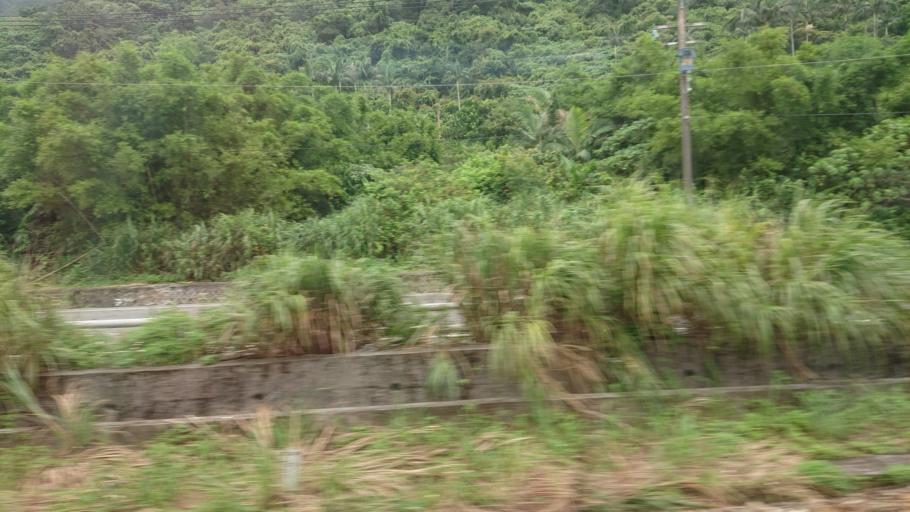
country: TW
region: Taiwan
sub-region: Keelung
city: Keelung
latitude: 24.9723
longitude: 121.9303
